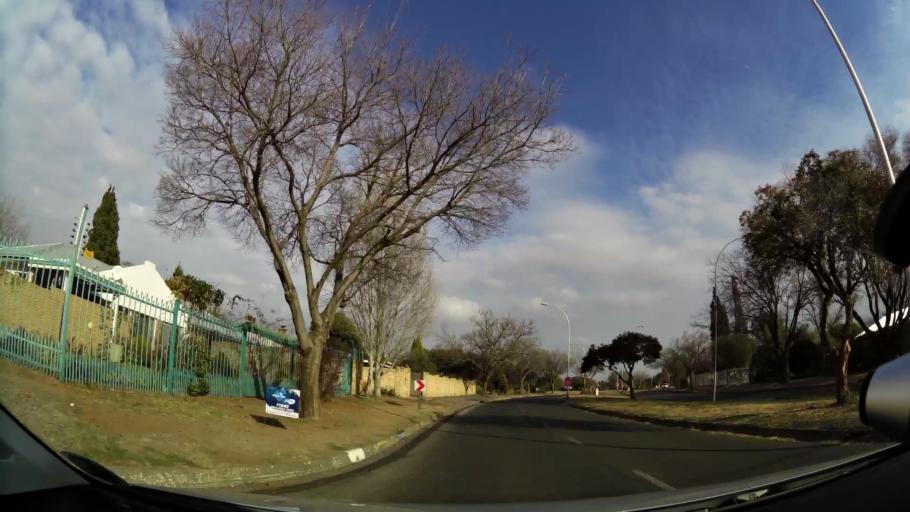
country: ZA
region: Orange Free State
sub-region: Mangaung Metropolitan Municipality
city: Bloemfontein
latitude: -29.1238
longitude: 26.1762
